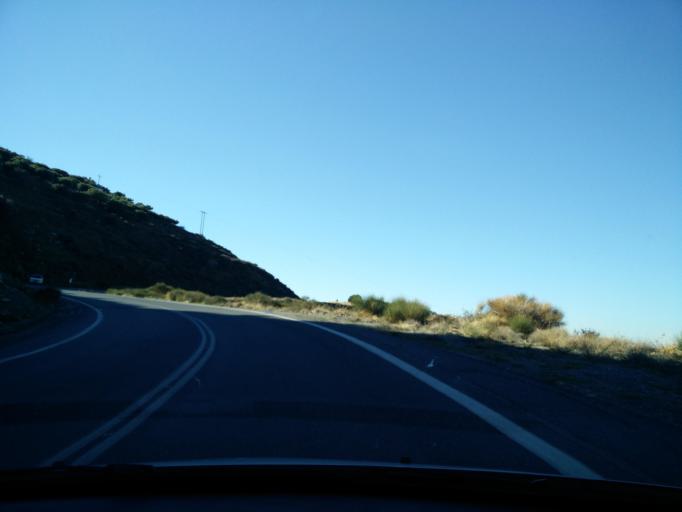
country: GR
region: Crete
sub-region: Nomos Irakleiou
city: Arkalochori
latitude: 35.0689
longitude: 25.3605
